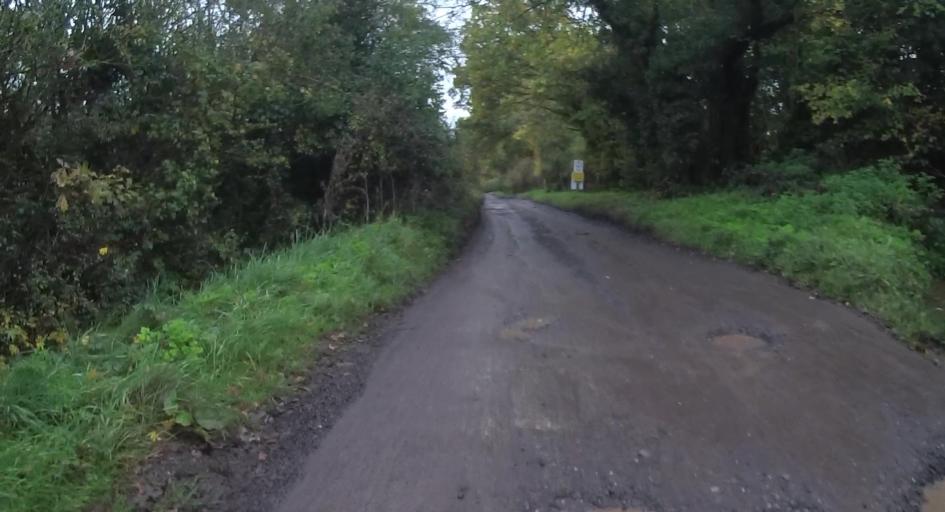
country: GB
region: England
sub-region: Surrey
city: Farnham
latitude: 51.2218
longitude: -0.8087
